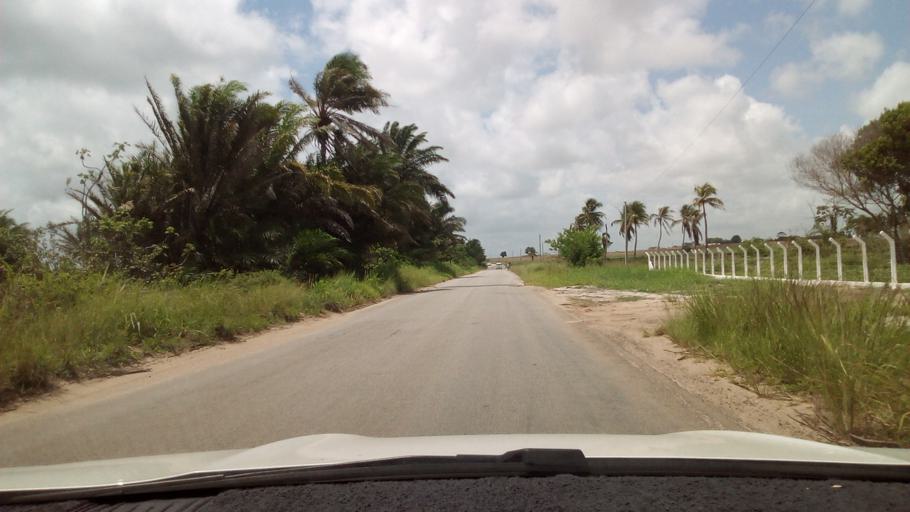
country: BR
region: Paraiba
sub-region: Alhandra
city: Alhandra
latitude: -7.4497
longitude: -34.9133
